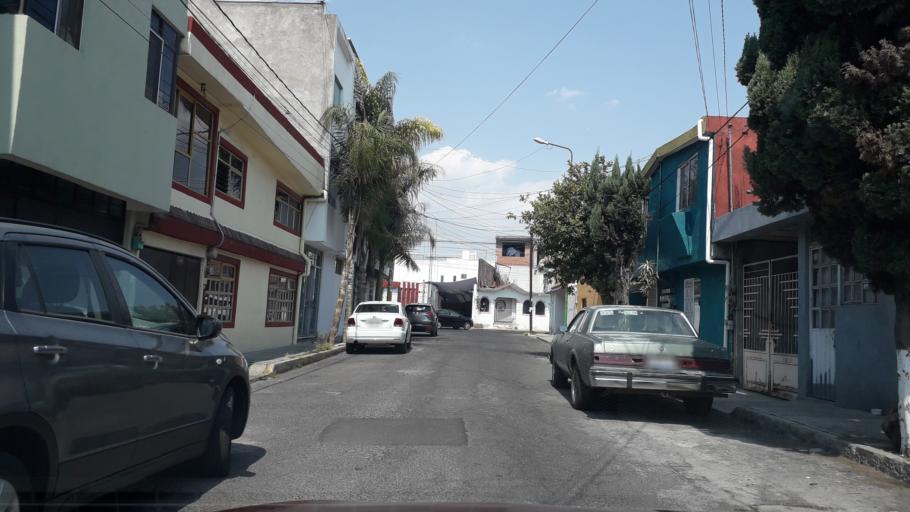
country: MX
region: Puebla
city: Puebla
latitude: 19.0434
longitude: -98.2294
